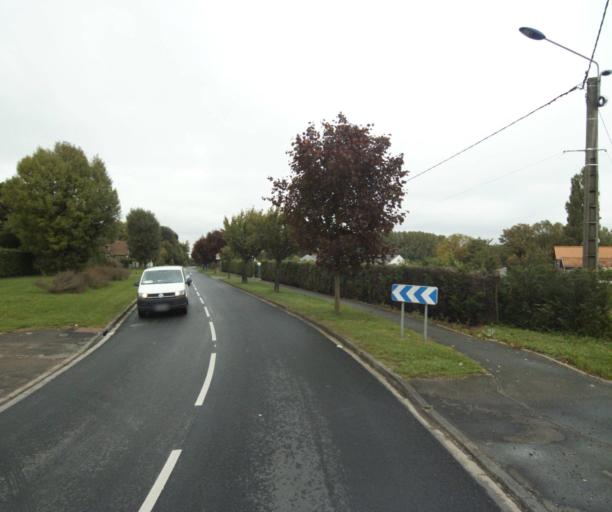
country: FR
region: Nord-Pas-de-Calais
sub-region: Departement du Nord
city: Wavrin
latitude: 50.5765
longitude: 2.9397
